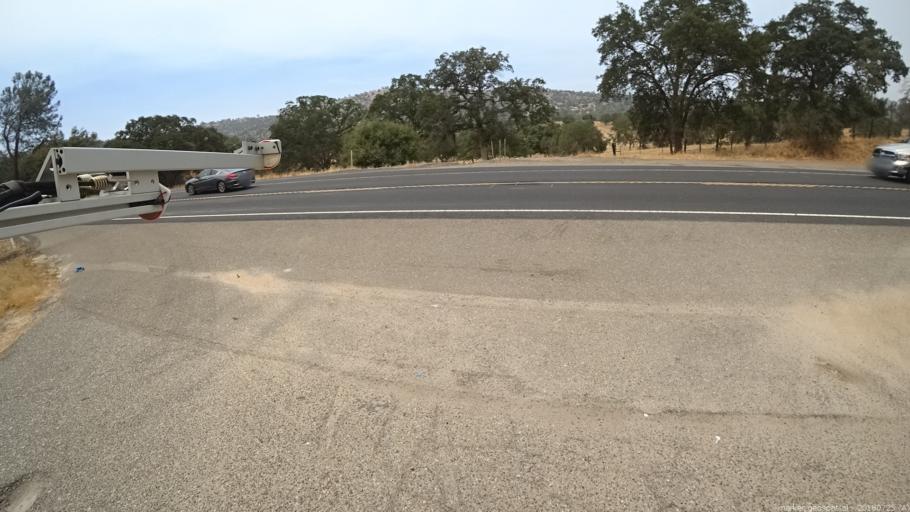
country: US
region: California
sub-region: Madera County
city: Yosemite Lakes
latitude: 37.1896
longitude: -119.7257
